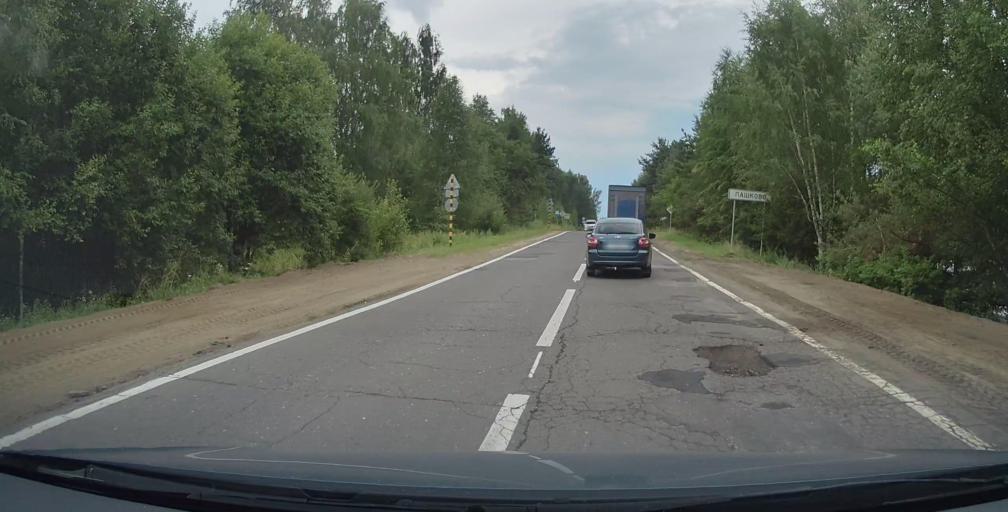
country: RU
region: Jaroslavl
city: Myshkin
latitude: 57.8548
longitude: 38.5101
